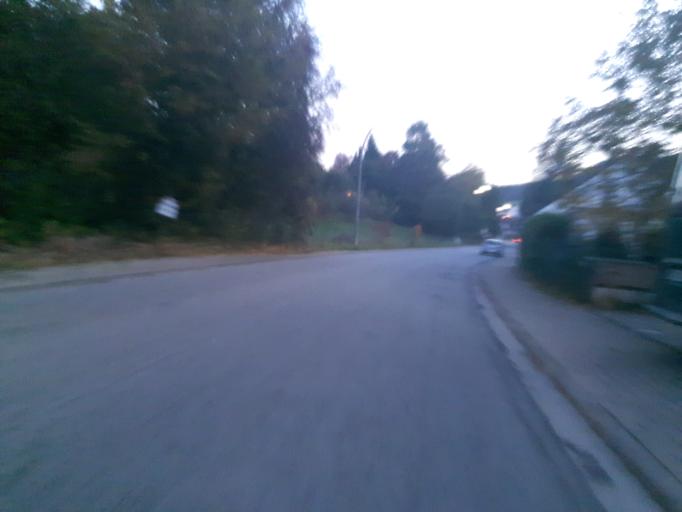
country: DE
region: Bavaria
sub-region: Regierungsbezirk Unterfranken
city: Leidersbach
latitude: 49.8848
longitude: 9.2421
